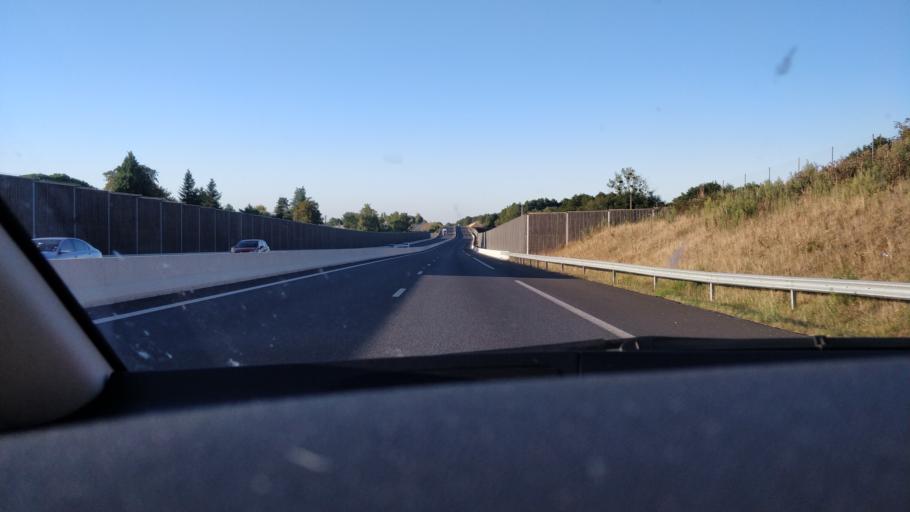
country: FR
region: Poitou-Charentes
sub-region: Departement de la Charente
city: Baignes-Sainte-Radegonde
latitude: 45.3960
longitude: -0.1791
